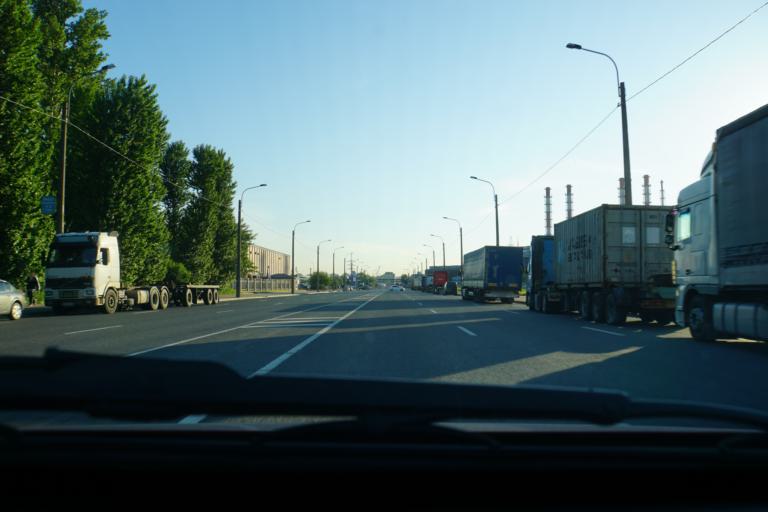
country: RU
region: St.-Petersburg
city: Avtovo
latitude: 59.8679
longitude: 30.2510
